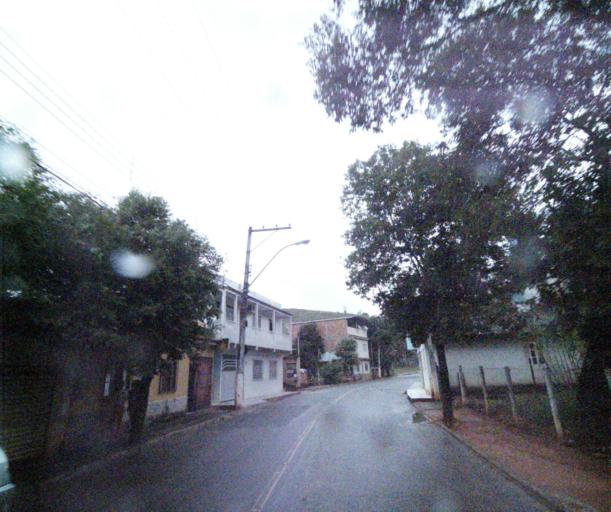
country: BR
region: Espirito Santo
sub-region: Muniz Freire
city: Muniz Freire
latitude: -20.4692
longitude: -41.4148
